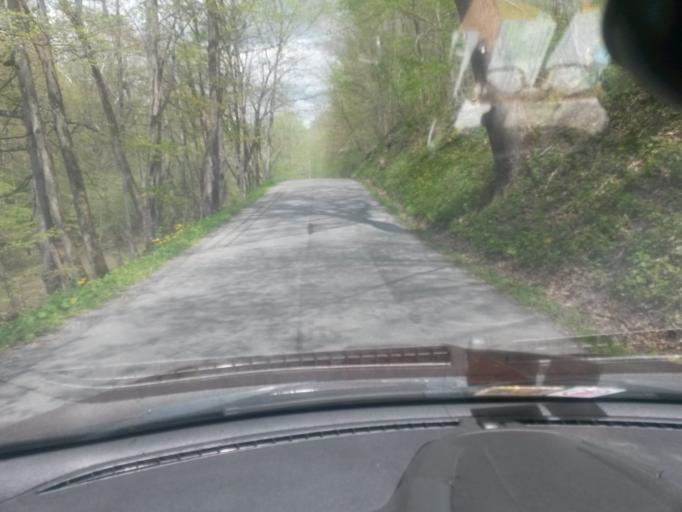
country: US
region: West Virginia
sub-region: Greenbrier County
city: White Sulphur Springs
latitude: 38.0455
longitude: -80.3490
